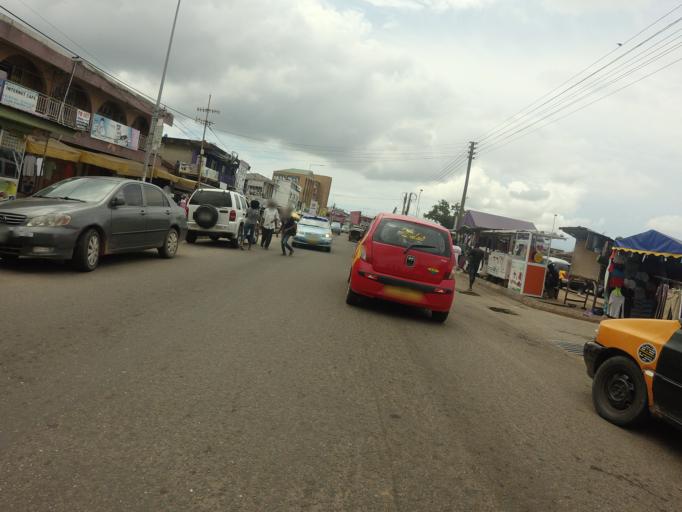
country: GH
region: Greater Accra
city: Accra
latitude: 5.5833
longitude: -0.2084
